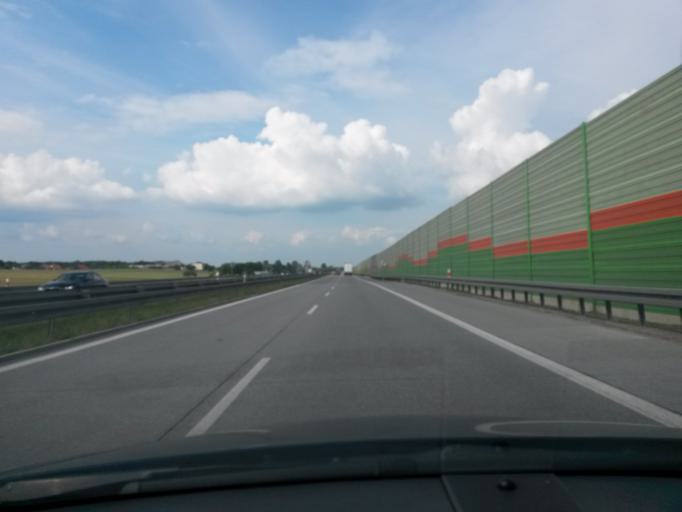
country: PL
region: Lodz Voivodeship
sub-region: Powiat tomaszowski
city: Lubochnia
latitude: 51.5994
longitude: 20.0572
